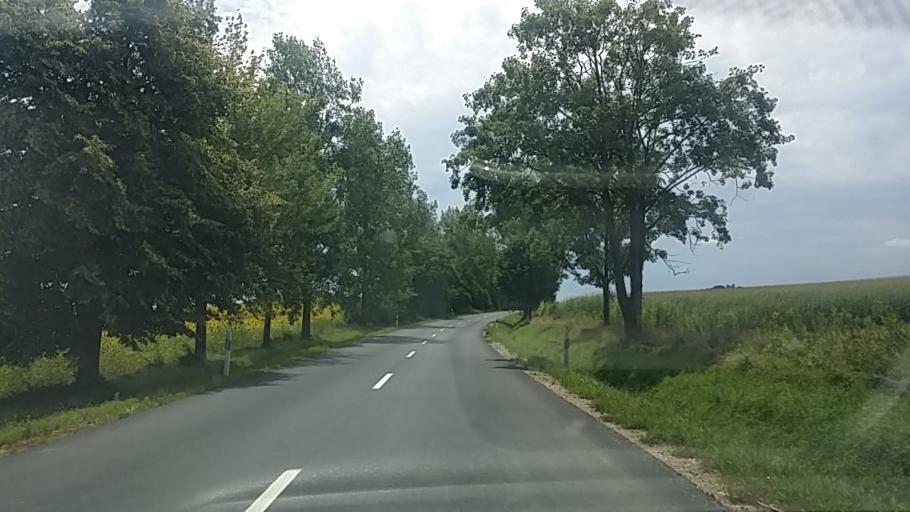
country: HR
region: Medimurska
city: Podturen
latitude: 46.5343
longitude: 16.5556
